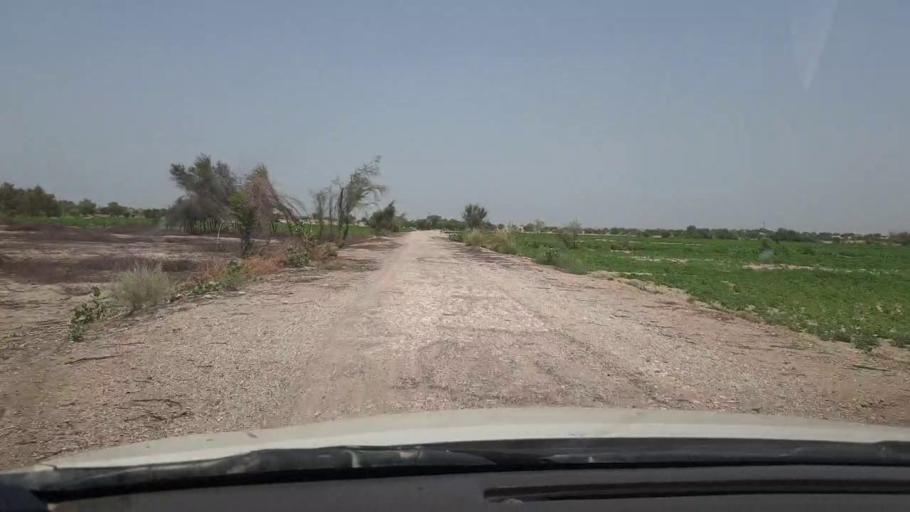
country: PK
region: Sindh
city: Rohri
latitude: 27.5116
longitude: 69.1845
